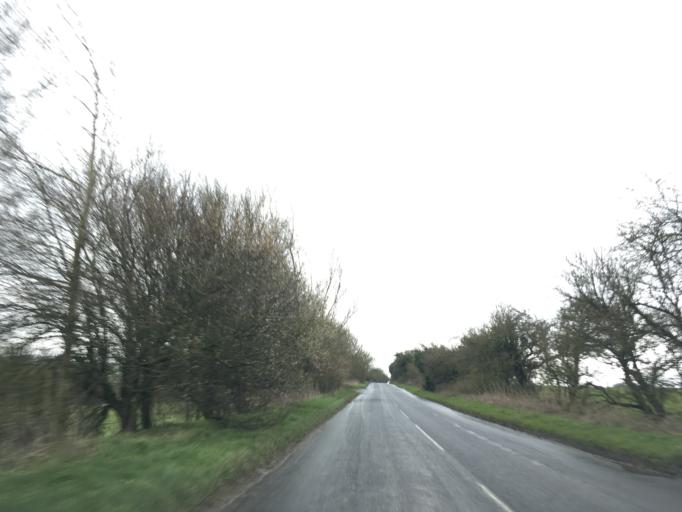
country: GB
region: England
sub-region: Borough of Swindon
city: Wanborough
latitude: 51.5425
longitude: -1.6848
